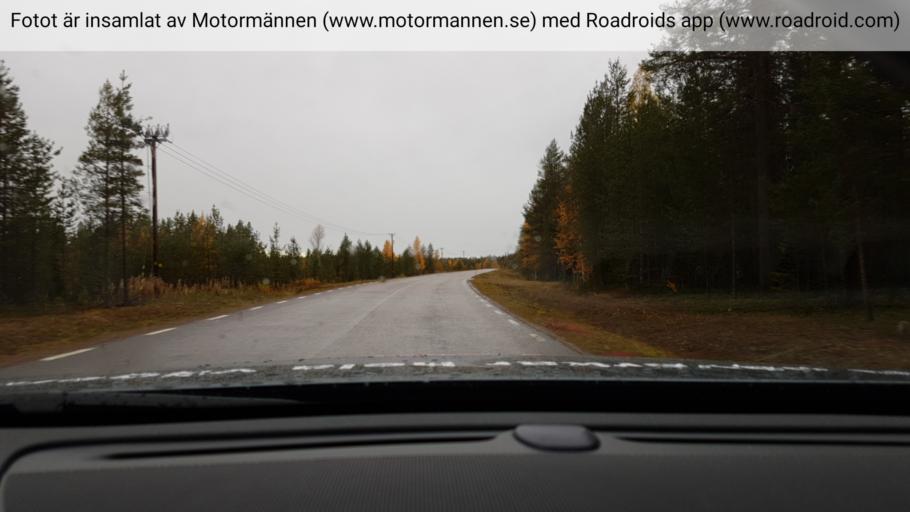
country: SE
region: Norrbotten
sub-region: Pajala Kommun
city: Pajala
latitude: 66.9255
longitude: 23.0008
